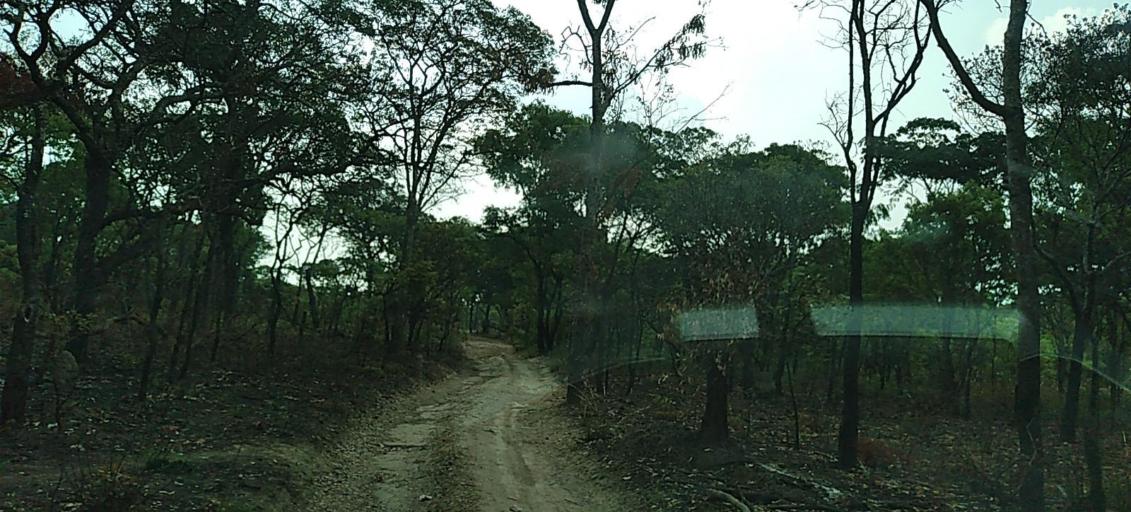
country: ZM
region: North-Western
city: Solwezi
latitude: -12.0777
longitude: 26.2431
